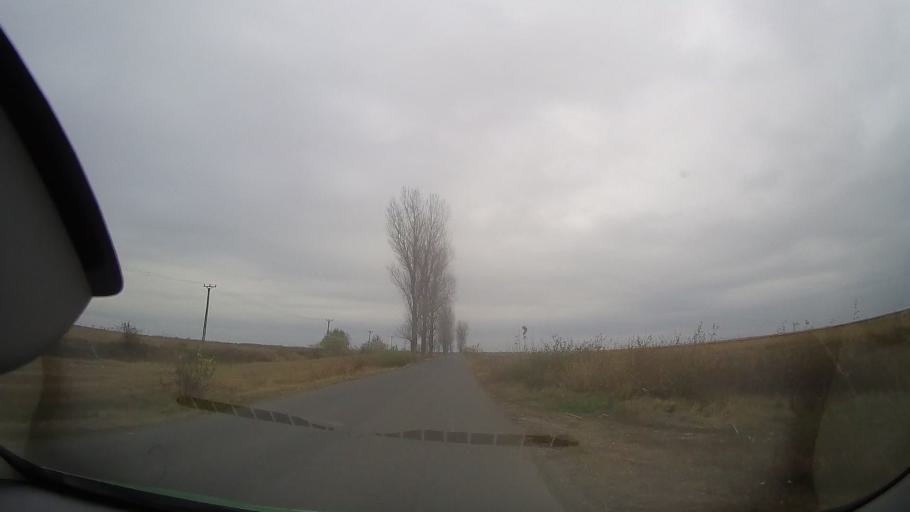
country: RO
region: Braila
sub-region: Comuna Rosiori
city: Rosiori
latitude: 44.8185
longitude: 27.3601
